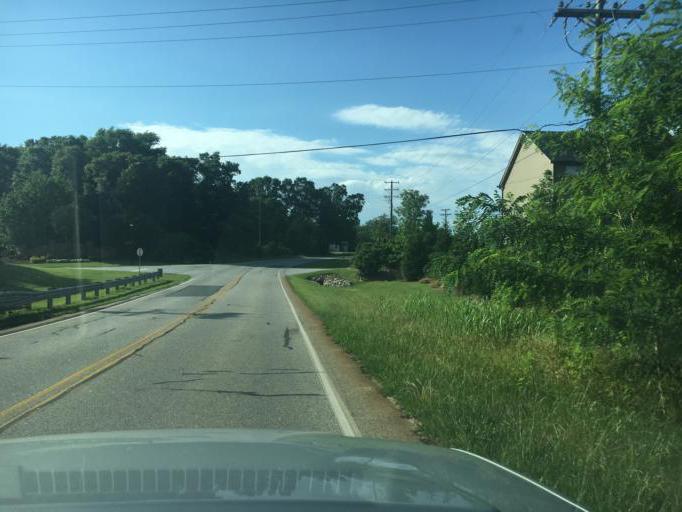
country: US
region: South Carolina
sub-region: Greenville County
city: Five Forks
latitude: 34.7941
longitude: -82.2308
